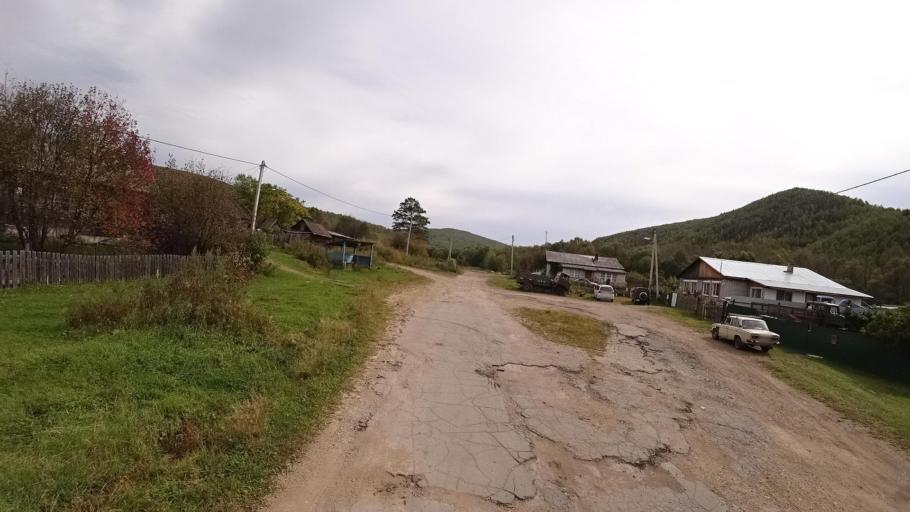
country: RU
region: Jewish Autonomous Oblast
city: Khingansk
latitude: 49.1220
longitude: 131.2057
